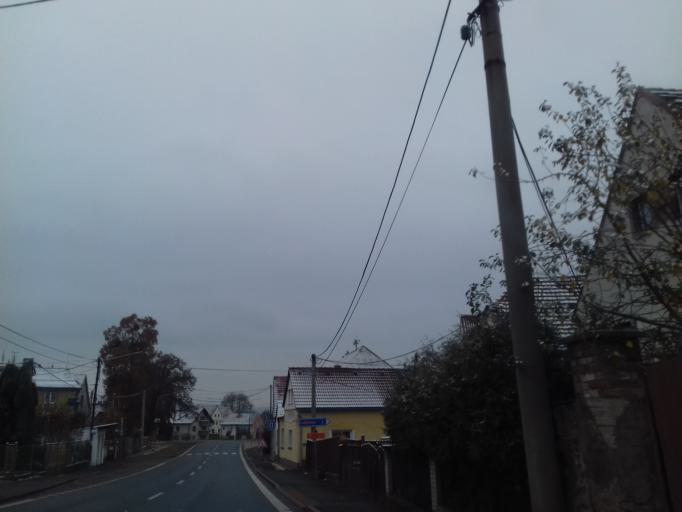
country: CZ
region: Plzensky
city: Meclov
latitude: 49.4551
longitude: 12.8728
